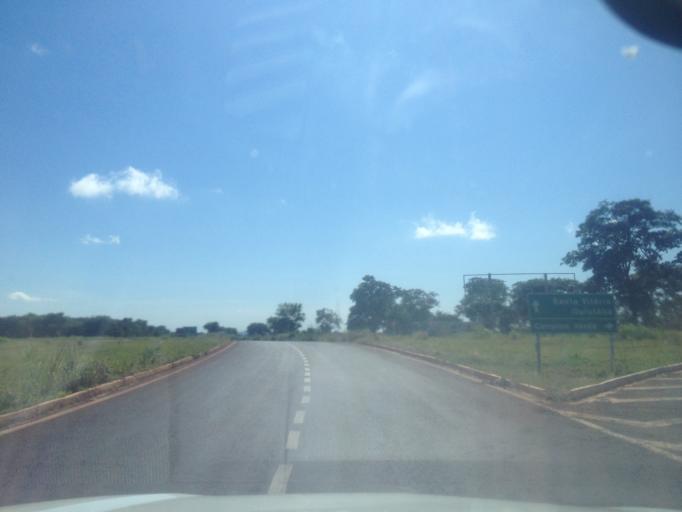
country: BR
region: Minas Gerais
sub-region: Santa Vitoria
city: Santa Vitoria
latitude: -19.0411
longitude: -50.4119
